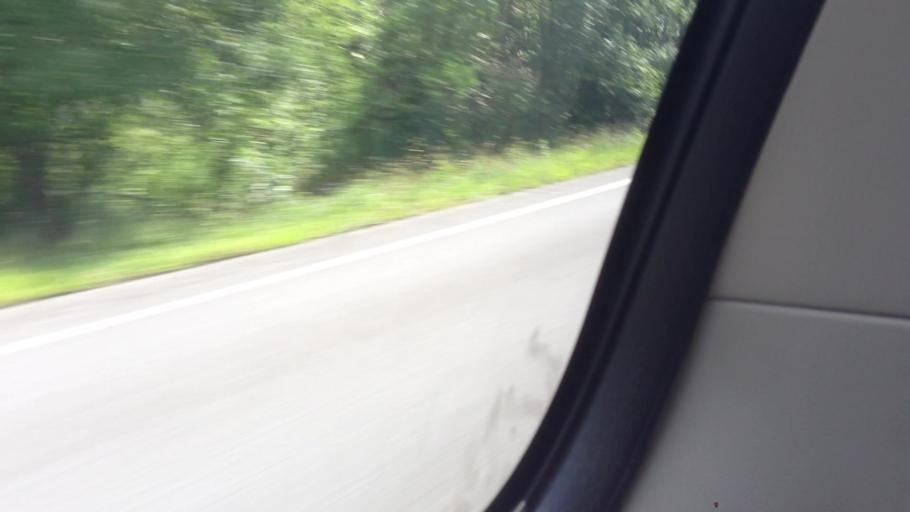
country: US
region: New York
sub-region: Dutchess County
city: Red Hook
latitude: 42.0163
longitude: -73.9054
